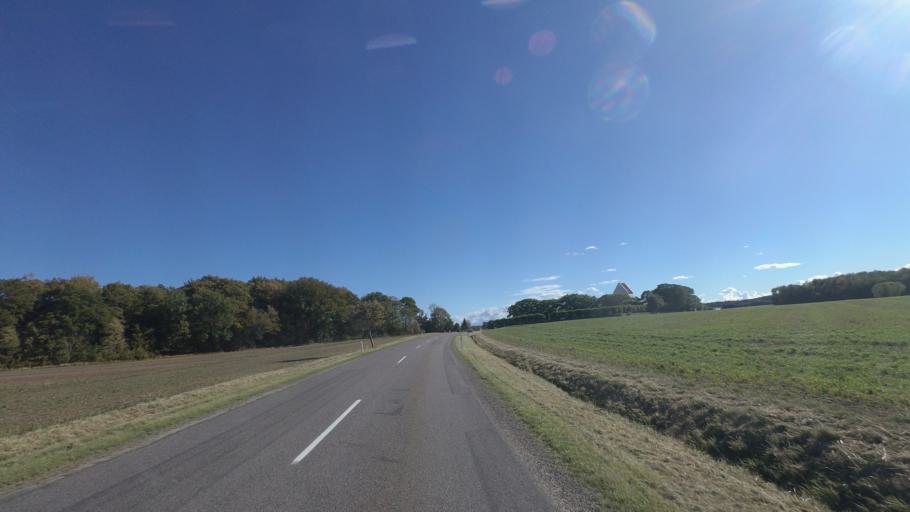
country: DK
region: Capital Region
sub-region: Bornholm Kommune
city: Nexo
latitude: 55.1194
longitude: 15.1039
